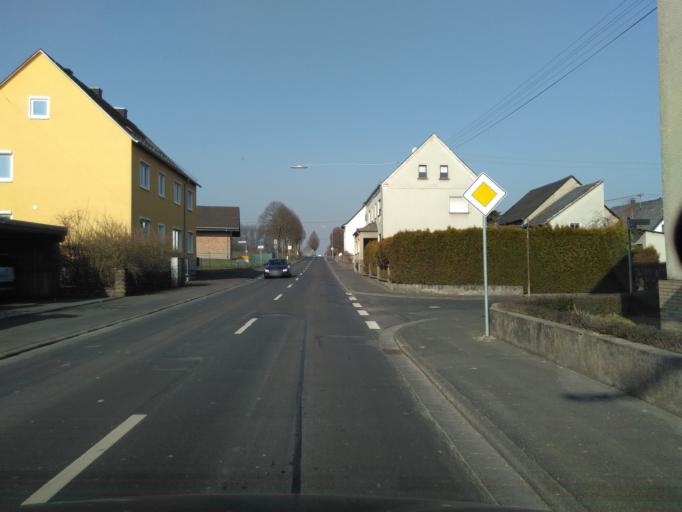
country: DE
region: Rheinland-Pfalz
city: Bannberscheid
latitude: 50.4659
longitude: 7.8246
